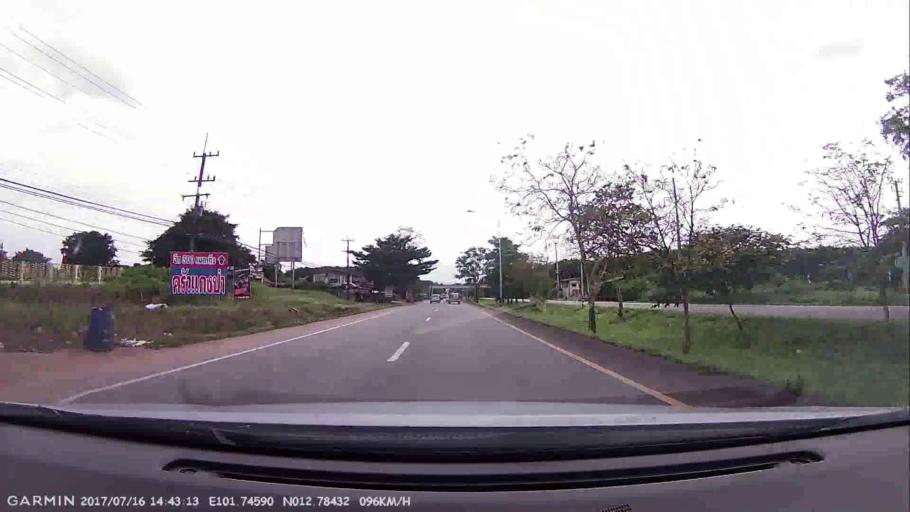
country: TH
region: Chanthaburi
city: Na Yai Am
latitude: 12.7842
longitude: 101.7456
